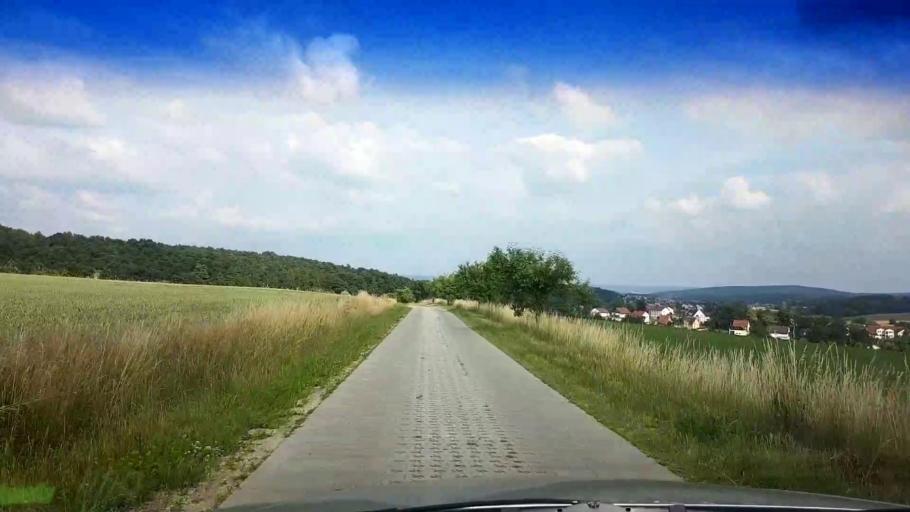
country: DE
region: Bavaria
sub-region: Upper Franconia
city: Walsdorf
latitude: 49.8746
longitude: 10.8082
